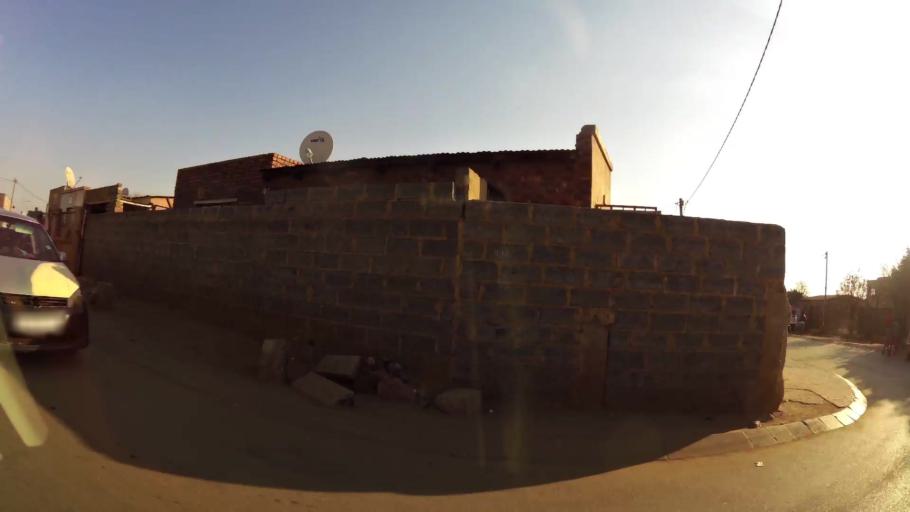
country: ZA
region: Gauteng
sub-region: Ekurhuleni Metropolitan Municipality
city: Tembisa
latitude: -25.9666
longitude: 28.2152
